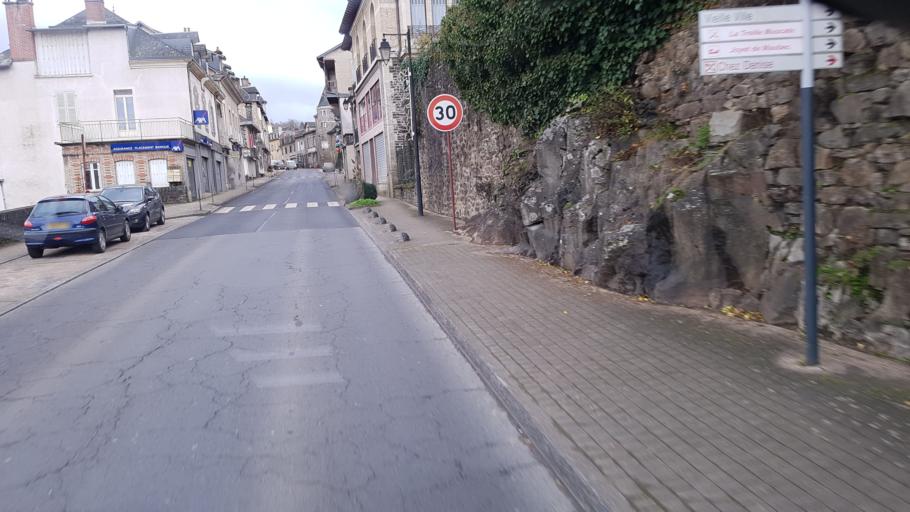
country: FR
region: Limousin
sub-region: Departement de la Correze
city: Uzerche
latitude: 45.4235
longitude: 1.5637
